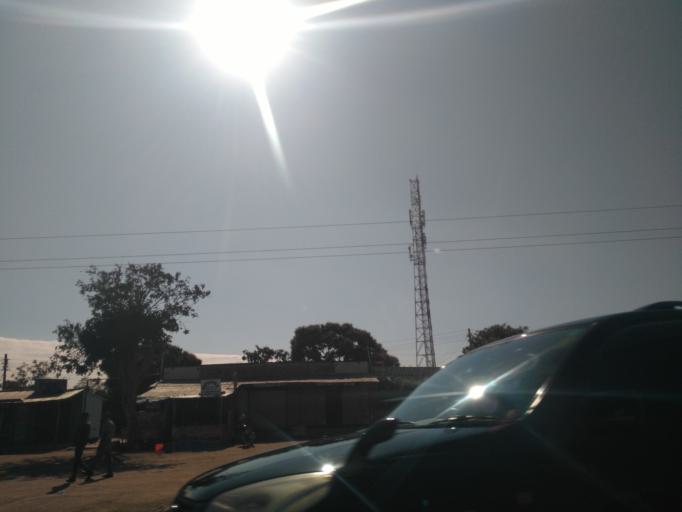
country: TZ
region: Dodoma
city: Dodoma
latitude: -6.1220
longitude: 35.7464
